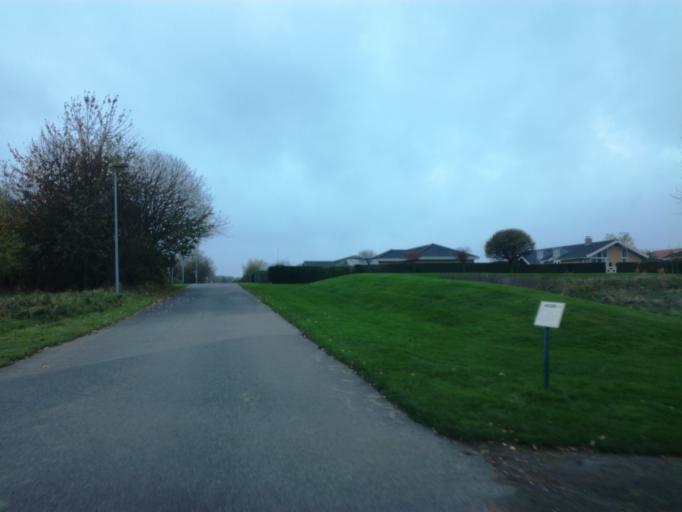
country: DK
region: South Denmark
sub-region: Fredericia Kommune
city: Fredericia
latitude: 55.5783
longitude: 9.7160
